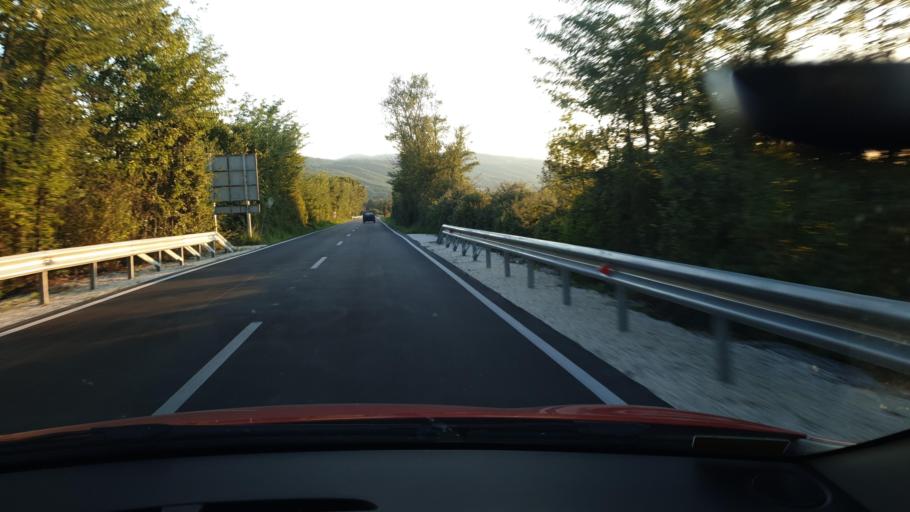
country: GR
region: Central Macedonia
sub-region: Nomos Chalkidikis
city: Polygyros
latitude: 40.4675
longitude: 23.3911
